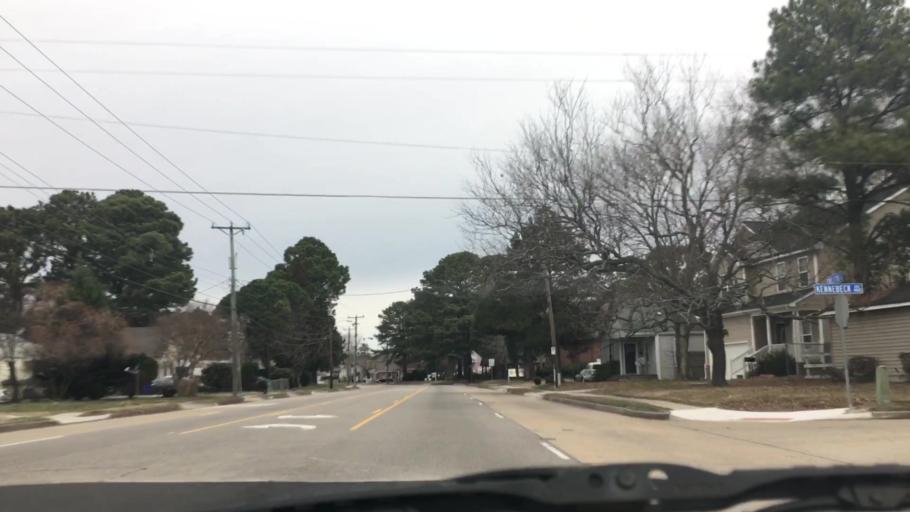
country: US
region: Virginia
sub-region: City of Norfolk
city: Norfolk
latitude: 36.8816
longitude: -76.2338
